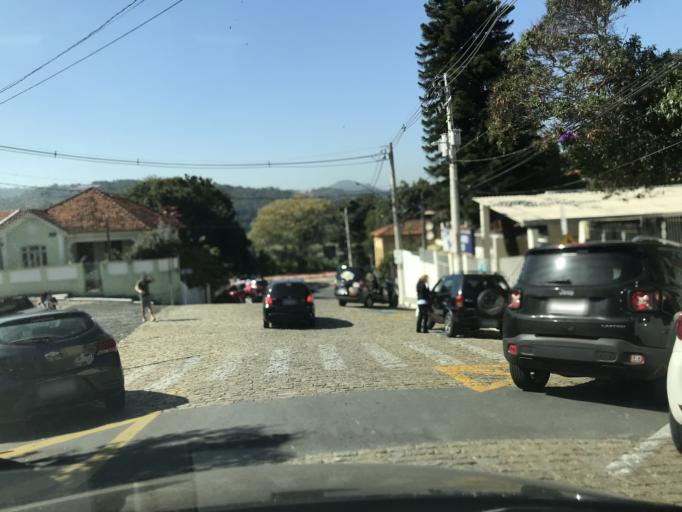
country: BR
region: Sao Paulo
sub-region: Santana De Parnaiba
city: Santana de Parnaiba
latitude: -23.4457
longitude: -46.9131
